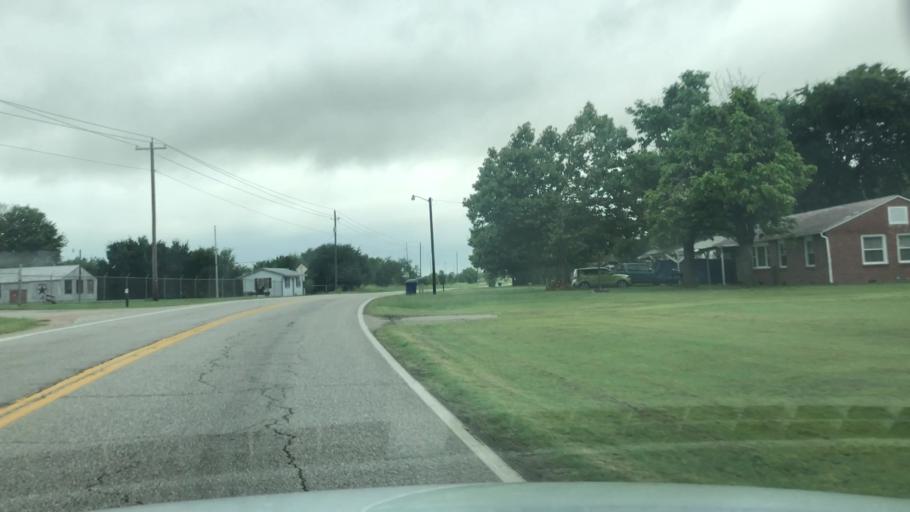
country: US
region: Oklahoma
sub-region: Nowata County
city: Nowata
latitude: 36.7029
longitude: -95.6483
